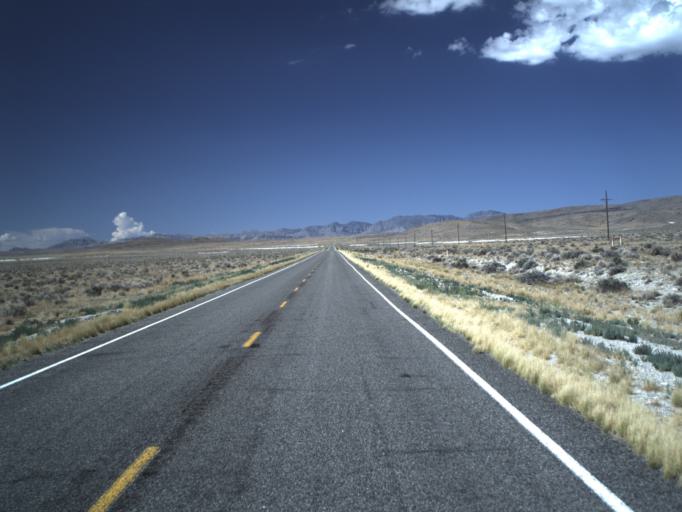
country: US
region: Utah
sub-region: Beaver County
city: Milford
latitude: 39.0691
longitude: -113.2251
